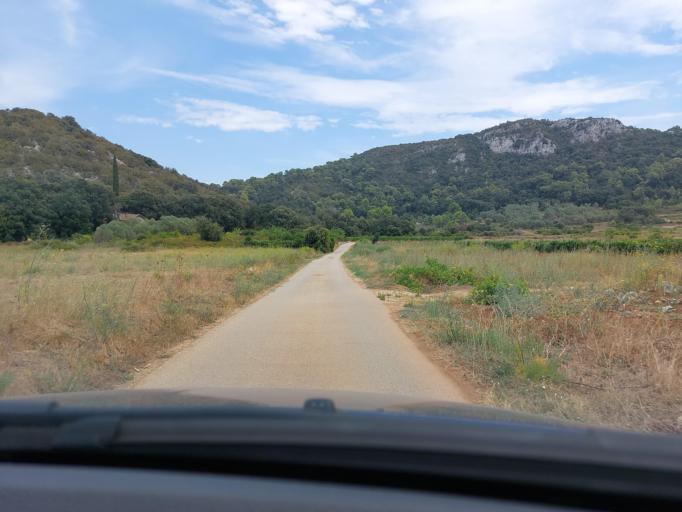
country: HR
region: Dubrovacko-Neretvanska
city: Smokvica
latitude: 42.7555
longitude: 16.9196
